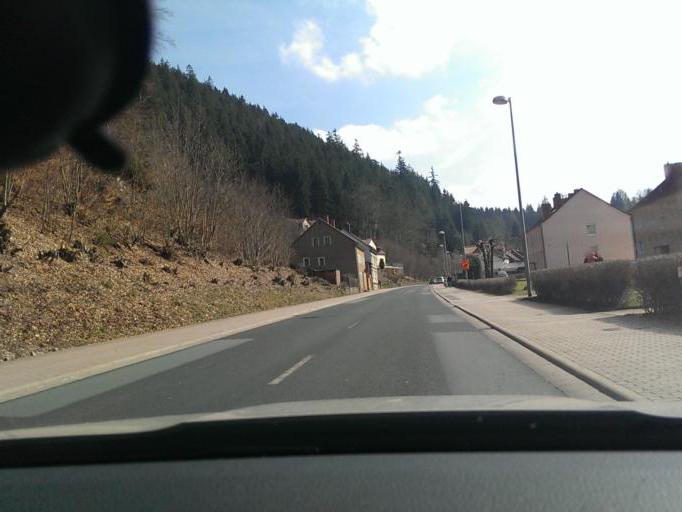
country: DE
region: Thuringia
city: Luisenthal
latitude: 50.7753
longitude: 10.7279
